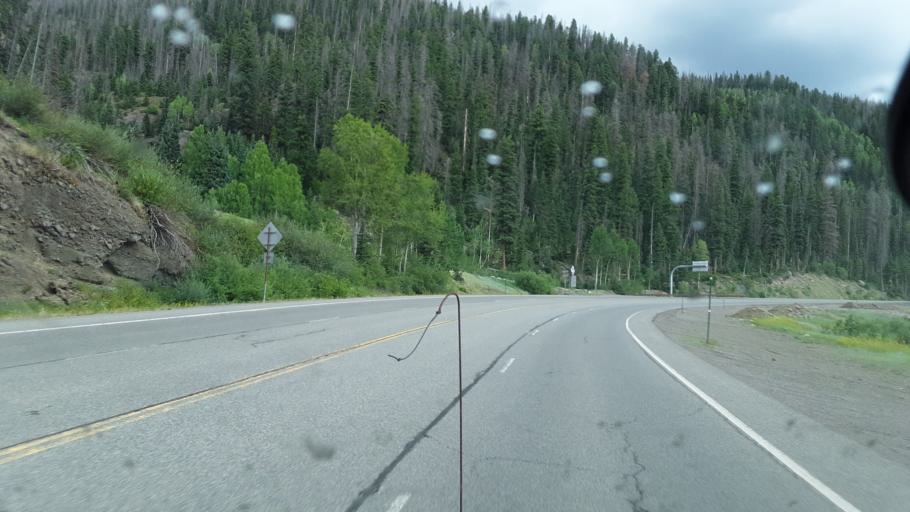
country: US
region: Colorado
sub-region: Archuleta County
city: Pagosa Springs
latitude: 37.4712
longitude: -106.8725
